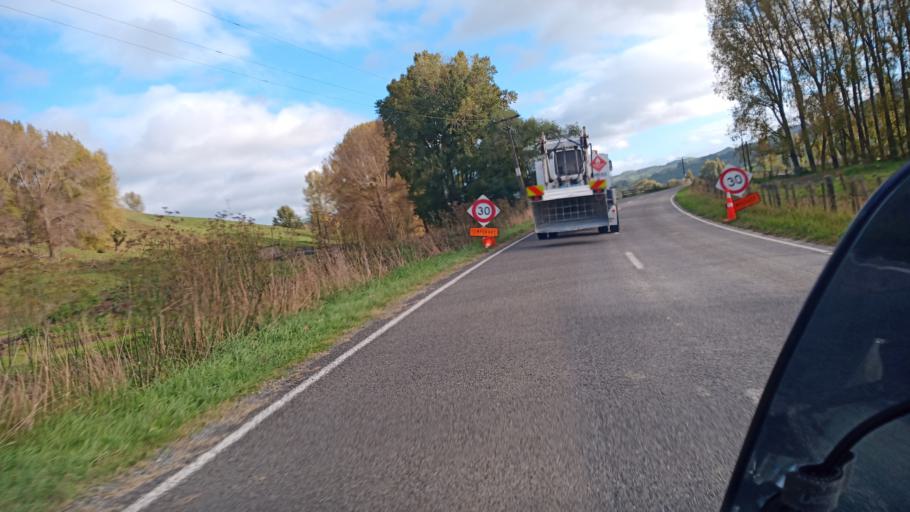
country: NZ
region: Gisborne
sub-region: Gisborne District
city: Gisborne
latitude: -38.5934
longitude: 177.7971
